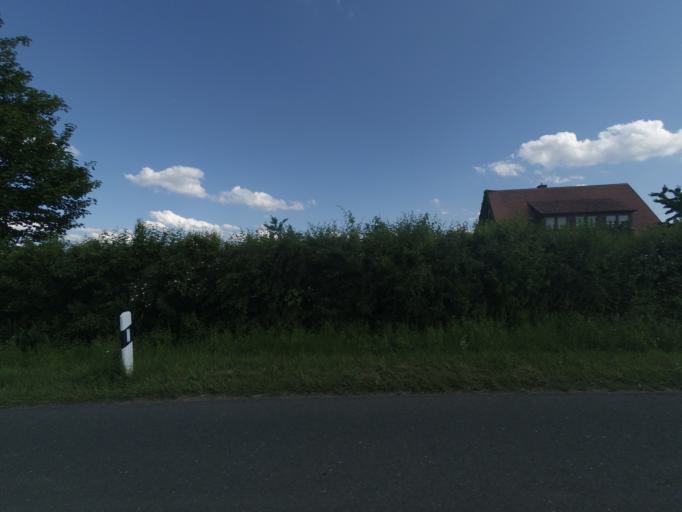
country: DE
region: Bavaria
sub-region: Regierungsbezirk Mittelfranken
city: Wilhermsdorf
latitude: 49.5145
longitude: 10.7168
